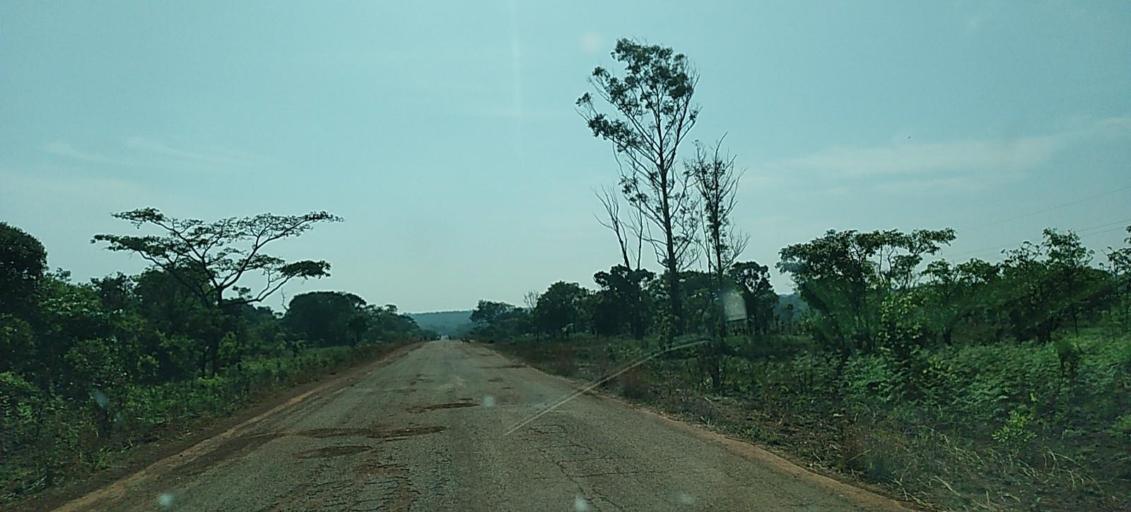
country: ZM
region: North-Western
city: Mwinilunga
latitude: -11.7864
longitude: 25.0305
